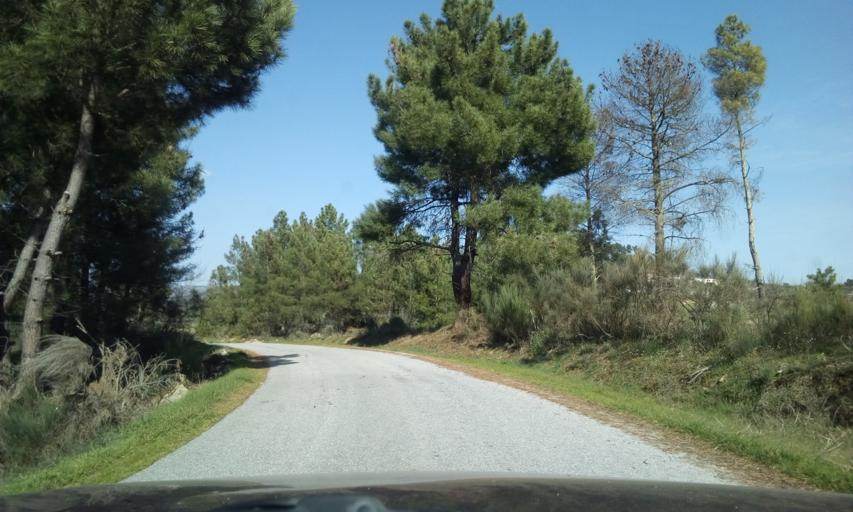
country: PT
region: Guarda
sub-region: Celorico da Beira
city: Celorico da Beira
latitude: 40.6527
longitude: -7.4149
